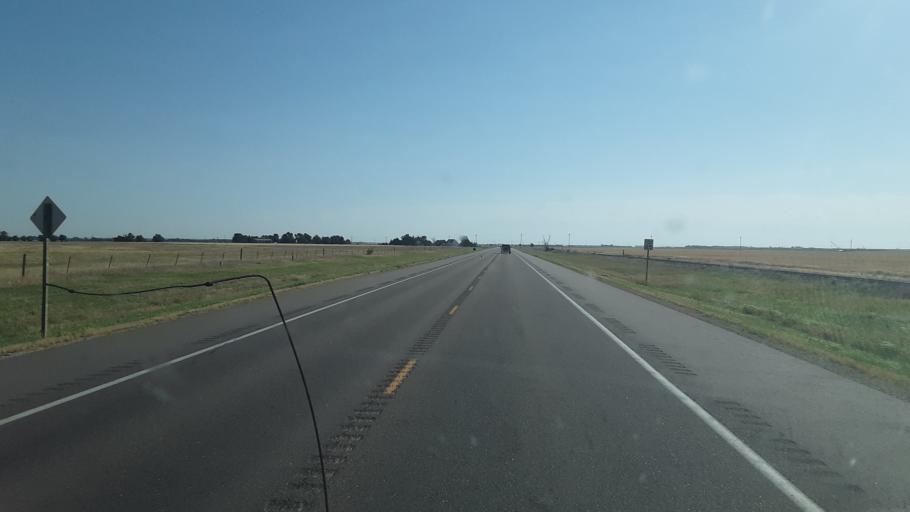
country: US
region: Kansas
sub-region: Pawnee County
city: Larned
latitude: 38.2047
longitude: -99.0643
